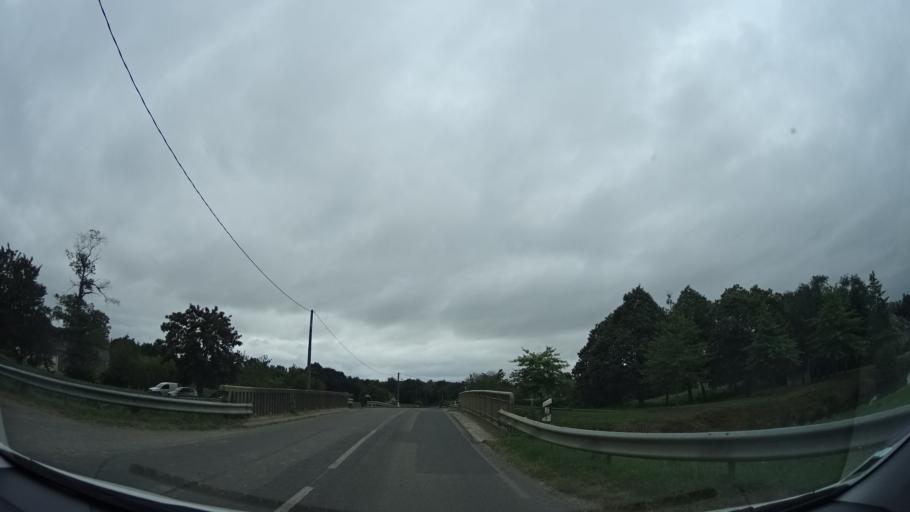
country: FR
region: Brittany
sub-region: Departement d'Ille-et-Vilaine
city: Quebriac
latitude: 48.3771
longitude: -1.8370
